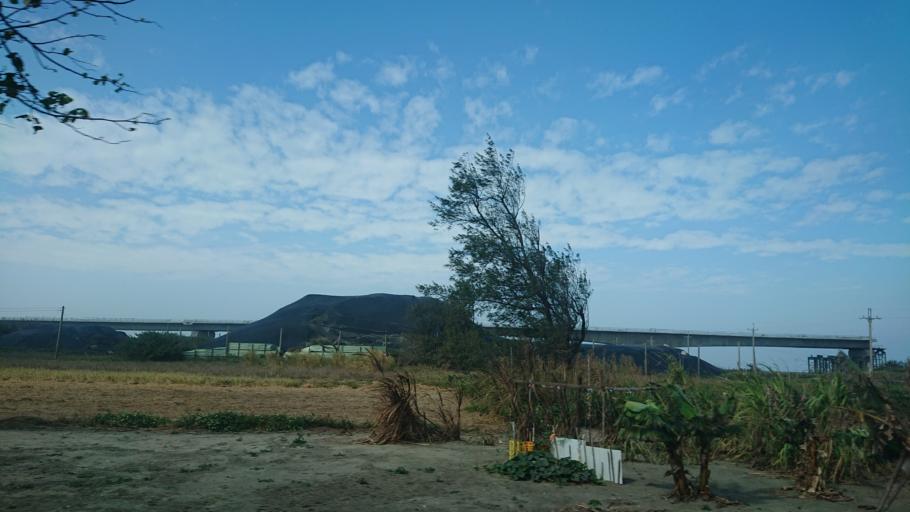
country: TW
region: Taiwan
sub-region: Changhua
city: Chang-hua
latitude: 23.9120
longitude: 120.3106
